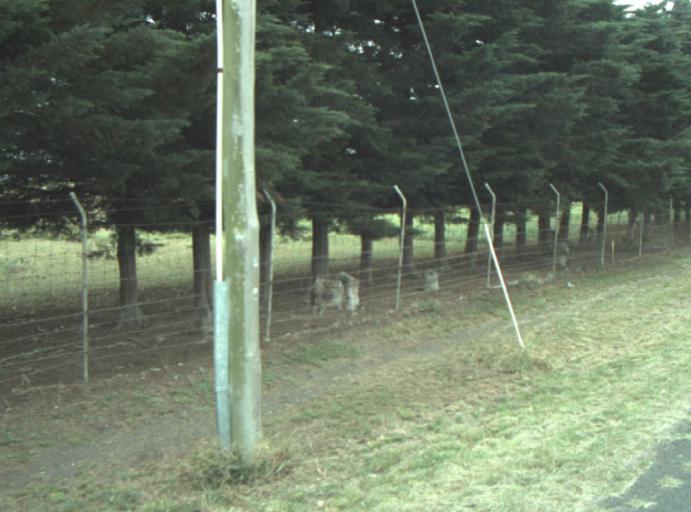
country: AU
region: Victoria
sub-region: Greater Geelong
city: Leopold
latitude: -38.1740
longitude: 144.4210
